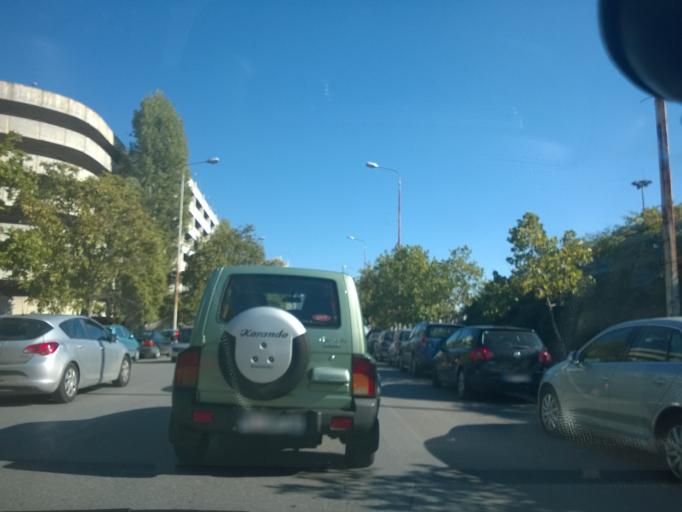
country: GR
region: Central Macedonia
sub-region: Nomos Thessalonikis
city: Thessaloniki
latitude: 40.6377
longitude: 22.9330
